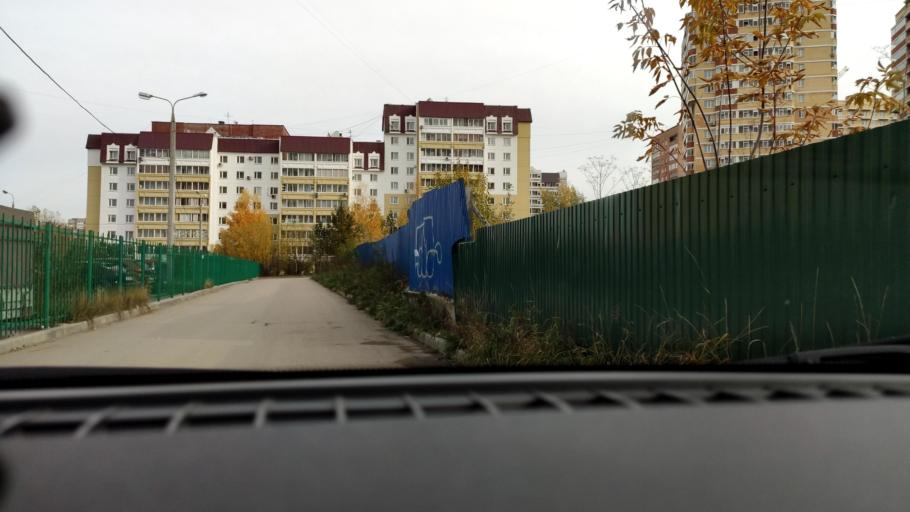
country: RU
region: Perm
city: Perm
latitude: 57.9990
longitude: 56.2025
